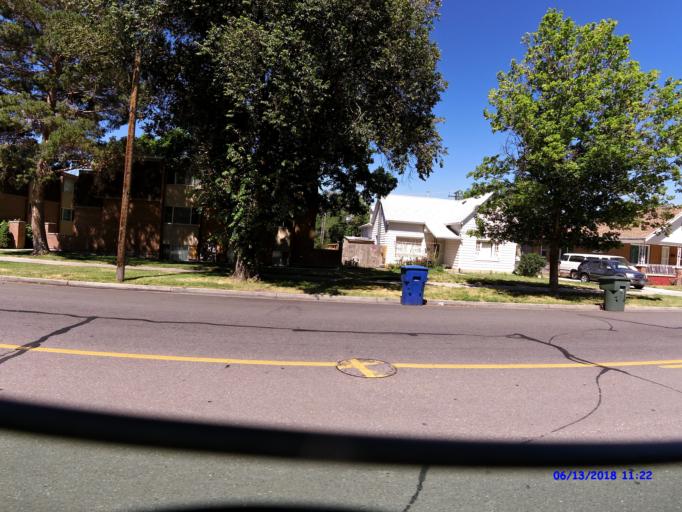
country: US
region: Utah
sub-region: Weber County
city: Ogden
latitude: 41.2260
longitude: -111.9592
